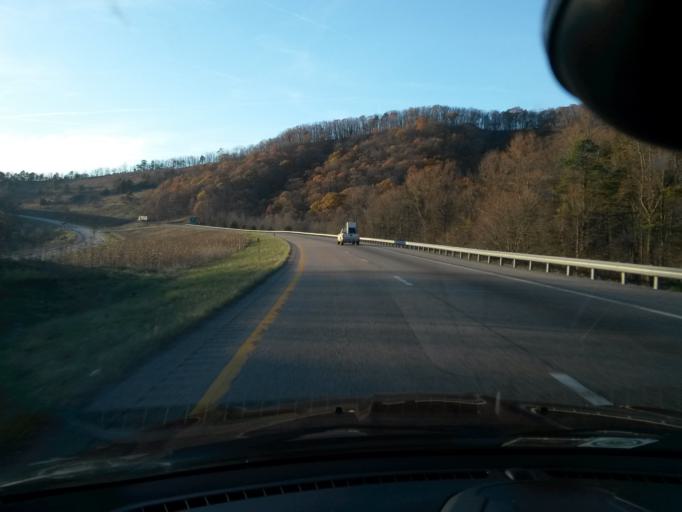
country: US
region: Virginia
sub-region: City of Lexington
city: Lexington
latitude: 37.8963
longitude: -79.5689
